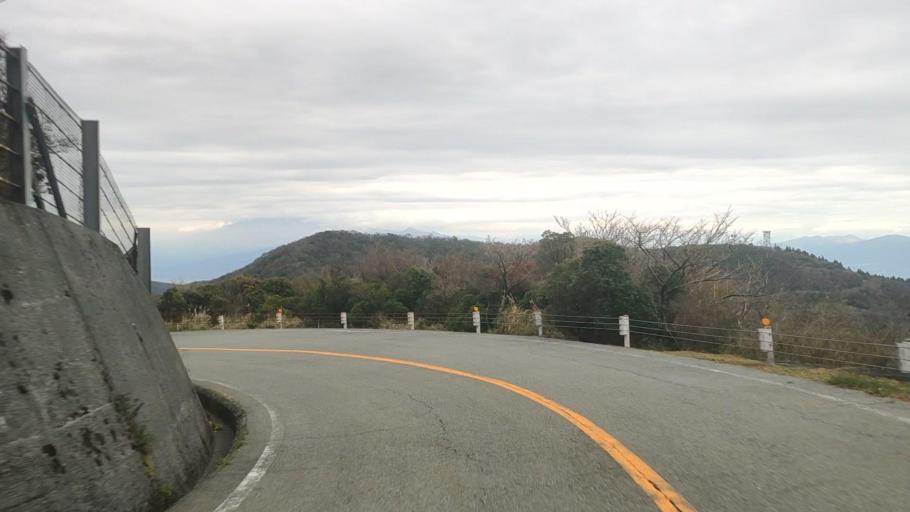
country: JP
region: Shizuoka
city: Heda
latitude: 34.9580
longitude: 138.8400
